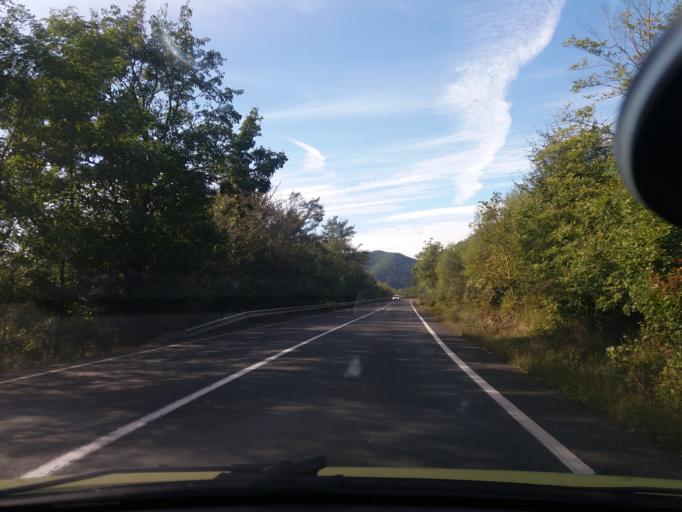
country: RO
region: Hunedoara
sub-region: Comuna Burjuc
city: Burjuc
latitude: 45.9435
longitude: 22.4991
